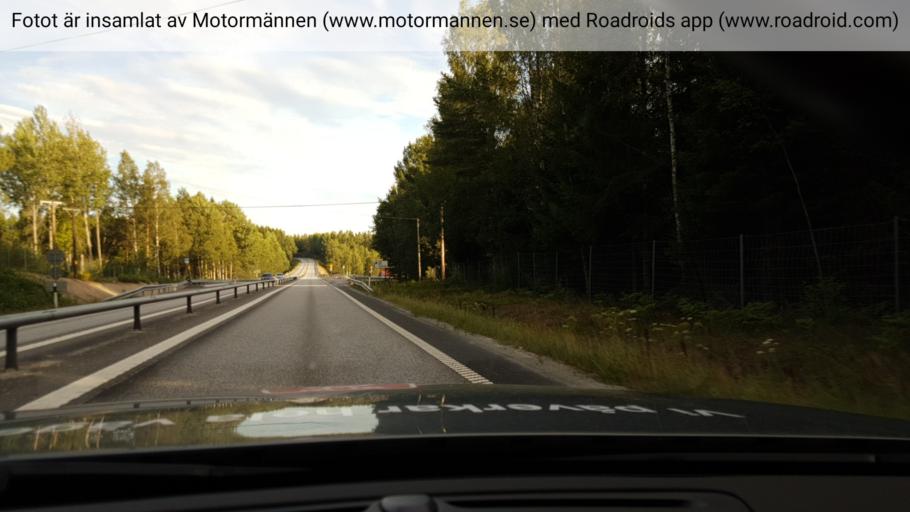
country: SE
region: OErebro
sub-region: Karlskoga Kommun
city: Karlskoga
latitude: 59.2911
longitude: 14.6794
